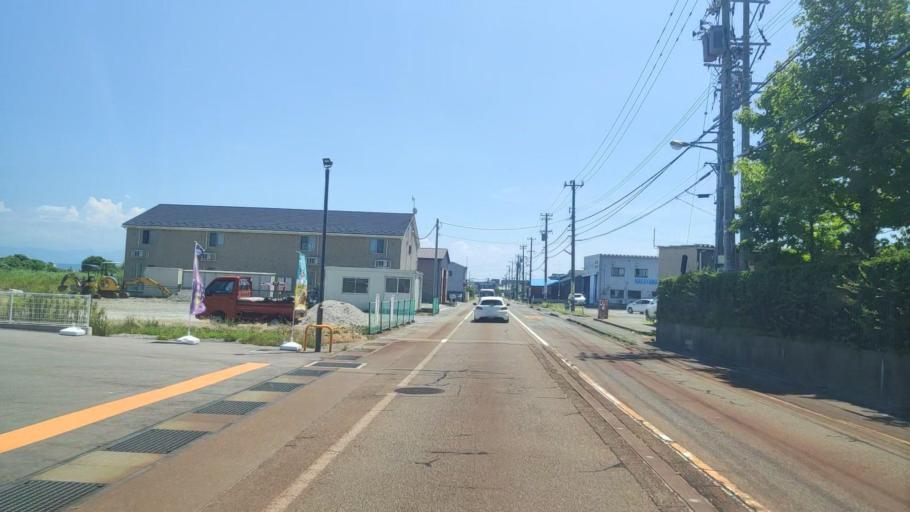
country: JP
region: Ishikawa
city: Kanazawa-shi
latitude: 36.6575
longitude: 136.6526
